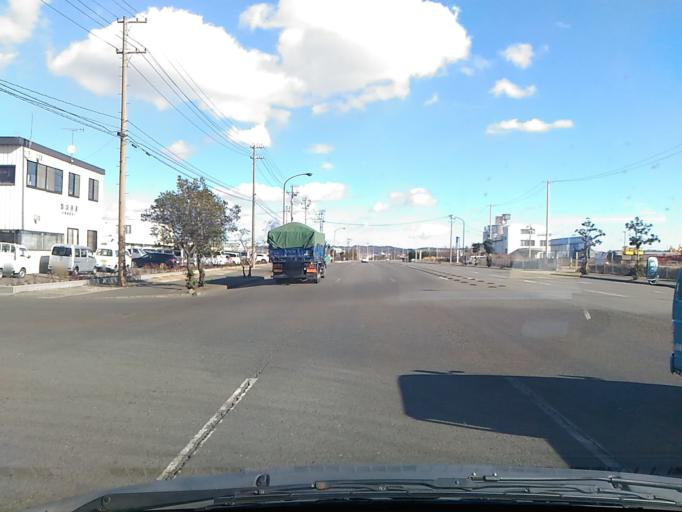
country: JP
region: Fukushima
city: Iwaki
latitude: 36.9399
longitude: 140.8855
